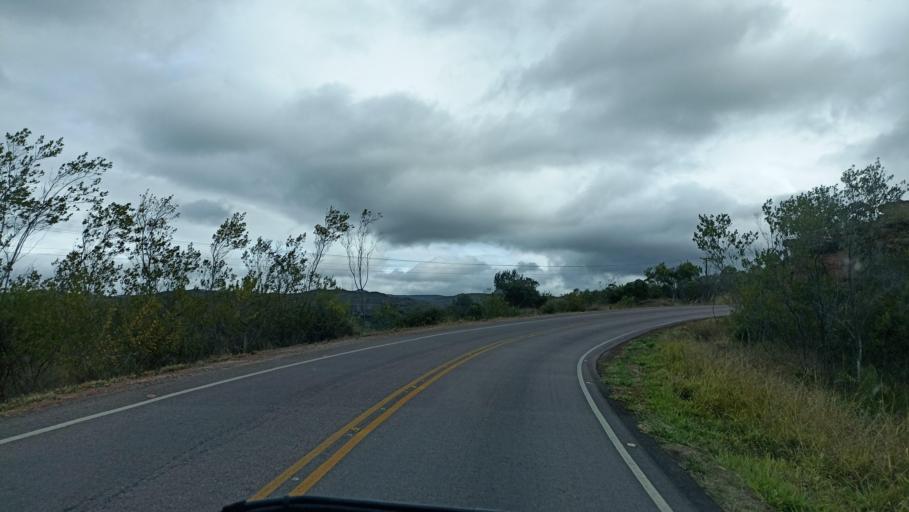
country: BR
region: Bahia
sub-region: Andarai
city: Vera Cruz
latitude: -12.9965
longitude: -41.3578
